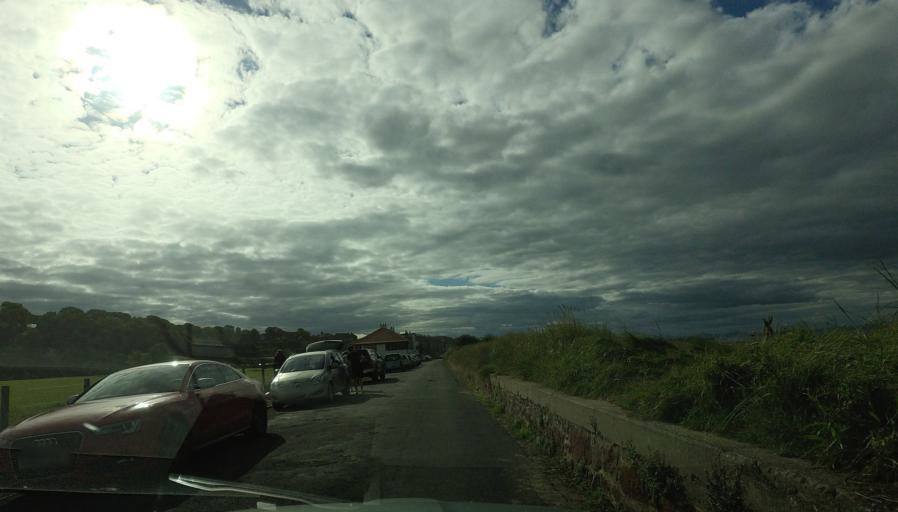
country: GB
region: Scotland
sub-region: East Lothian
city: North Berwick
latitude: 56.0574
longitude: -2.7006
